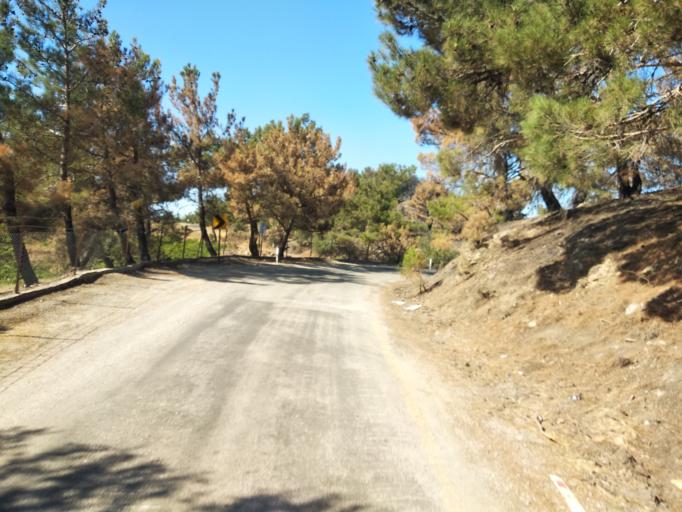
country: TR
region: Izmir
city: Gaziemir
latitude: 38.3051
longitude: 26.9990
